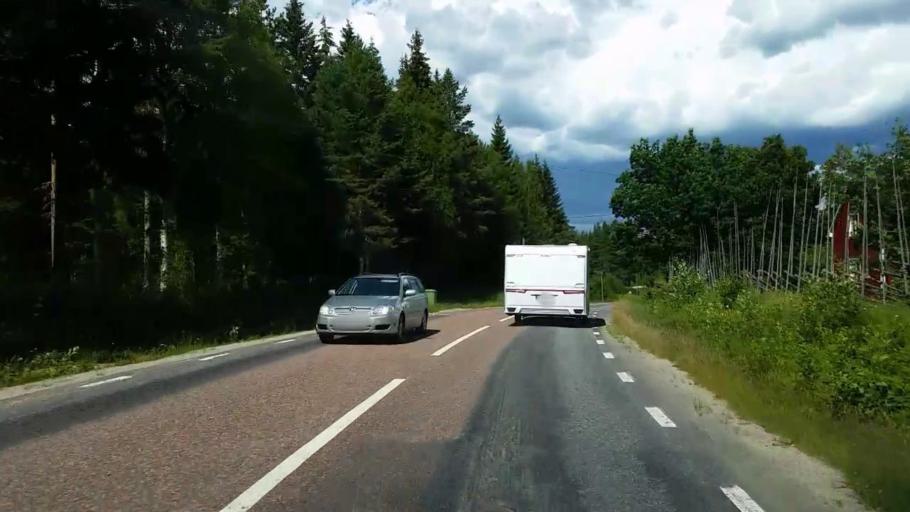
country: SE
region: Gaevleborg
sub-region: Ovanakers Kommun
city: Edsbyn
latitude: 61.3089
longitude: 15.5050
